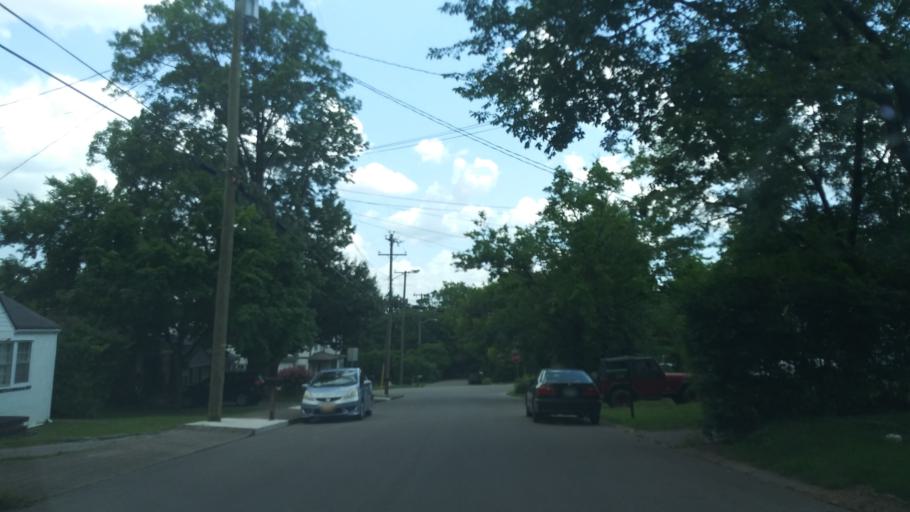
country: US
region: Tennessee
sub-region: Davidson County
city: Nashville
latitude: 36.1458
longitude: -86.8301
